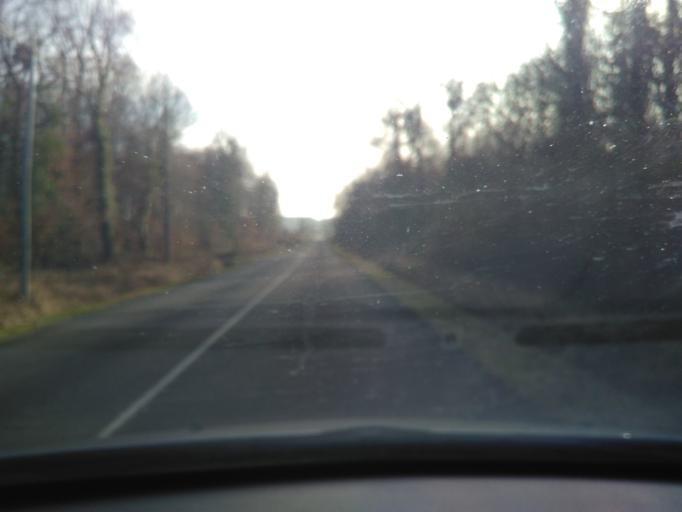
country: FR
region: Bourgogne
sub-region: Departement de la Nievre
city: Dornes
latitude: 46.7836
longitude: 3.2769
